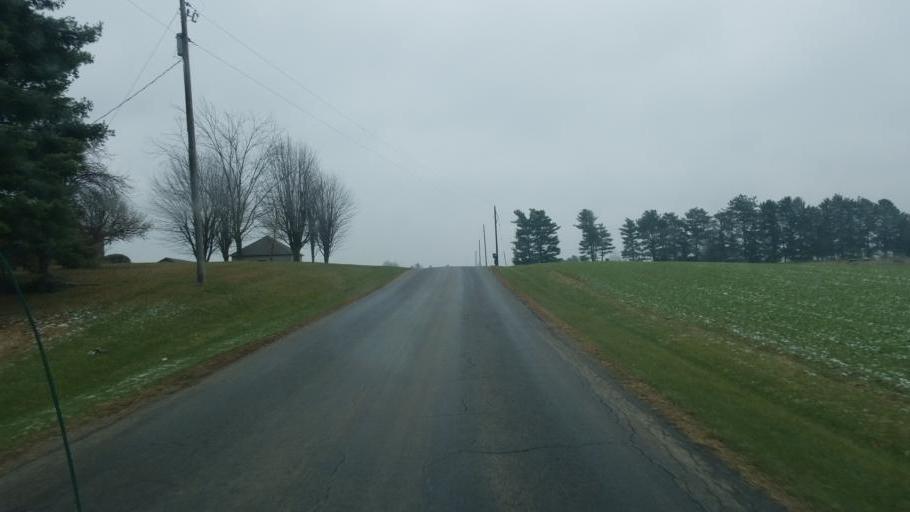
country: US
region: Ohio
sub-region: Huron County
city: Greenwich
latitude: 40.9755
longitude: -82.5426
